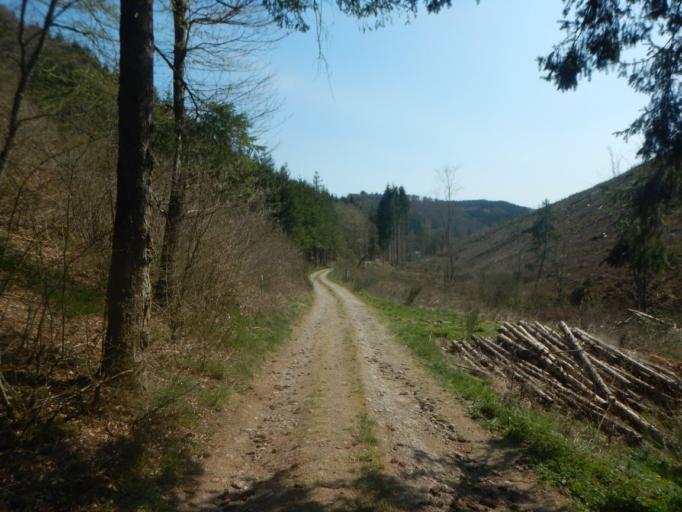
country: LU
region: Diekirch
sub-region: Canton de Clervaux
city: Clervaux
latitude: 50.0418
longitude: 6.0071
